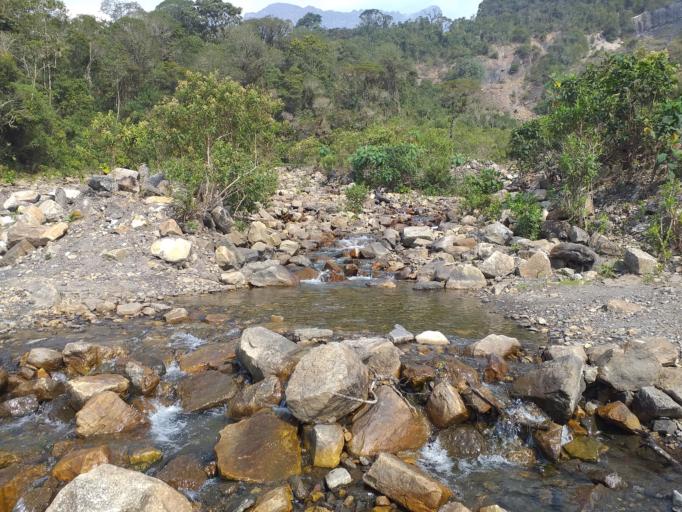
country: CO
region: Boyaca
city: Aquitania
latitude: 5.3826
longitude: -72.9266
